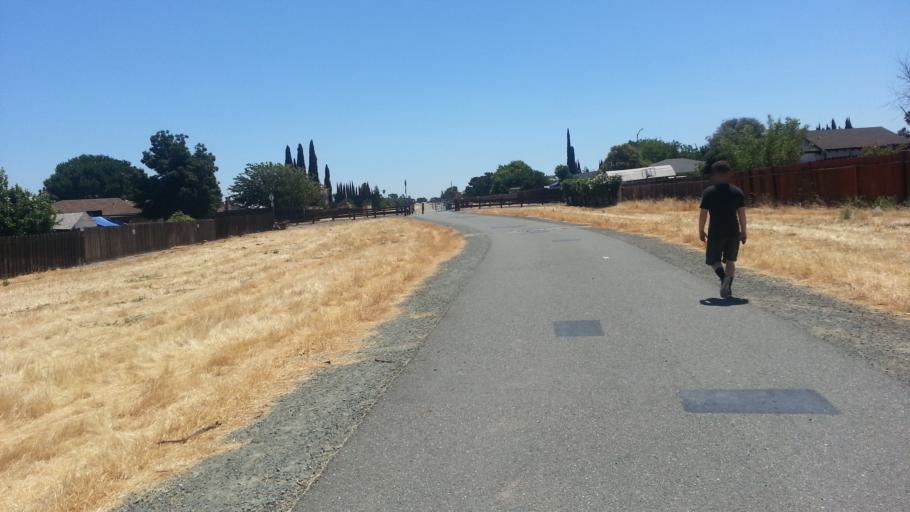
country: US
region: California
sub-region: Contra Costa County
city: Pittsburg
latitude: 38.0134
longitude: -121.9055
